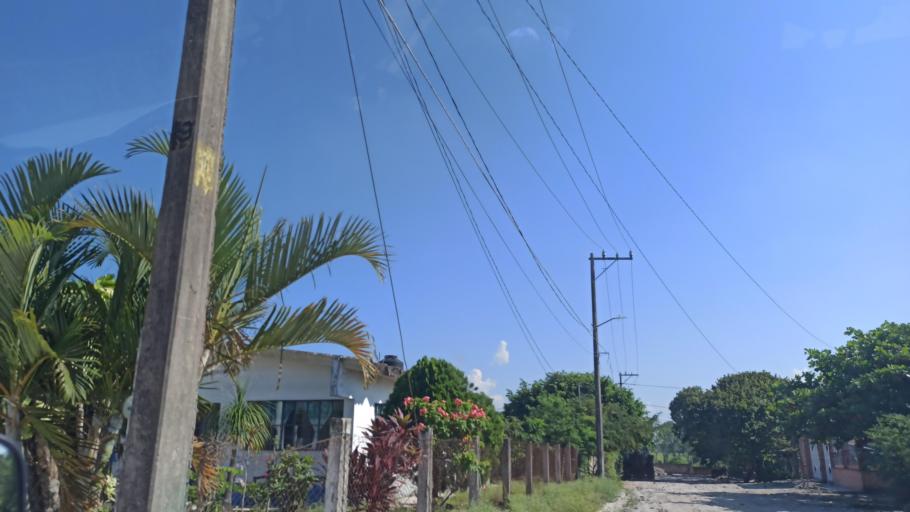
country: MX
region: Veracruz
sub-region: Martinez de la Torre
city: La Union Paso Largo
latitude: 20.1418
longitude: -97.0002
